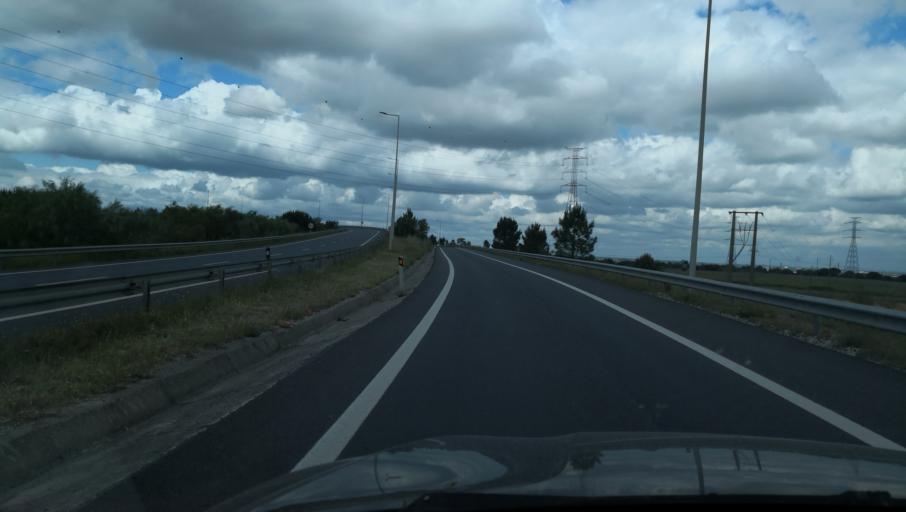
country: PT
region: Setubal
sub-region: Palmela
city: Palmela
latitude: 38.5786
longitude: -8.8629
